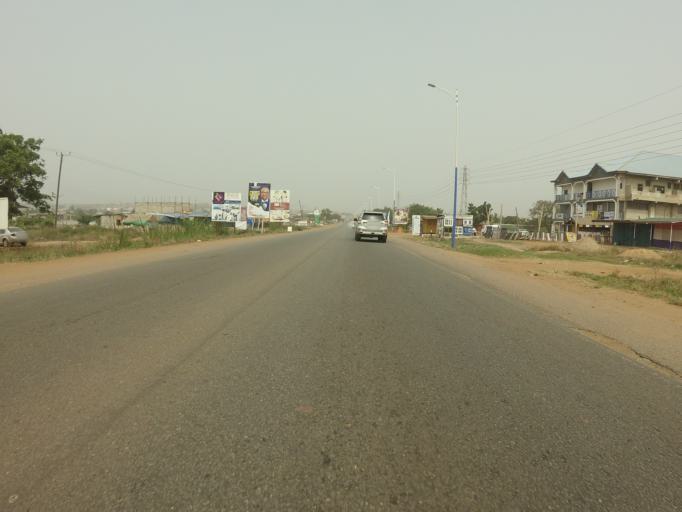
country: GH
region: Greater Accra
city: Tema
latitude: 5.7569
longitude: 0.0486
